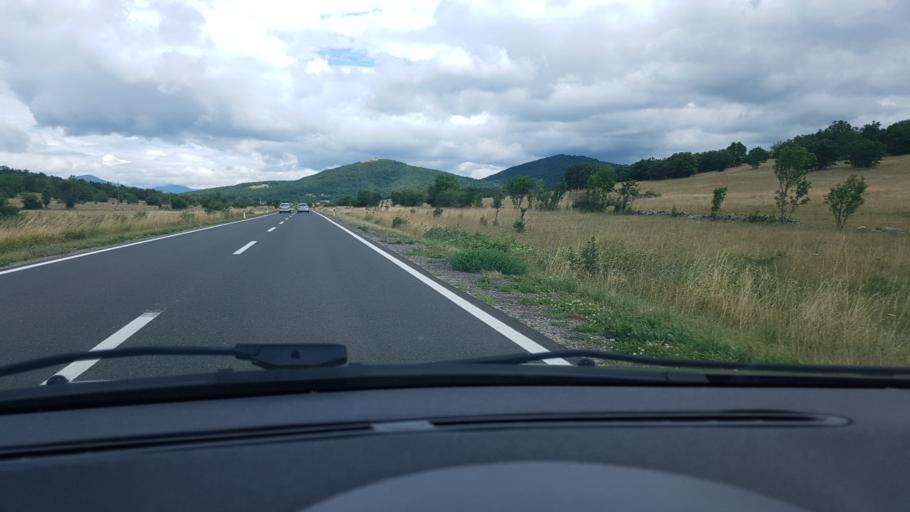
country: HR
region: Zadarska
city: Gracac
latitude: 44.4693
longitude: 15.7963
